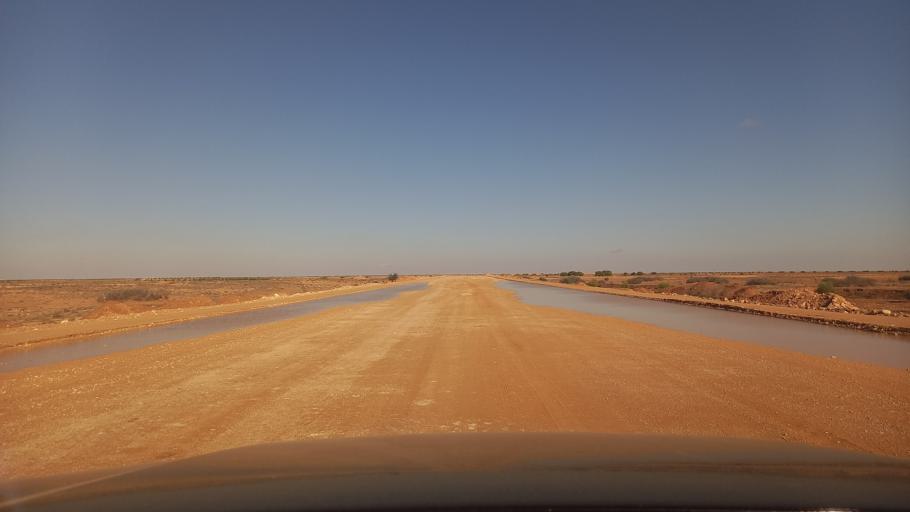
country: TN
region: Tataouine
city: Tataouine
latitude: 33.1377
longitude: 10.5052
